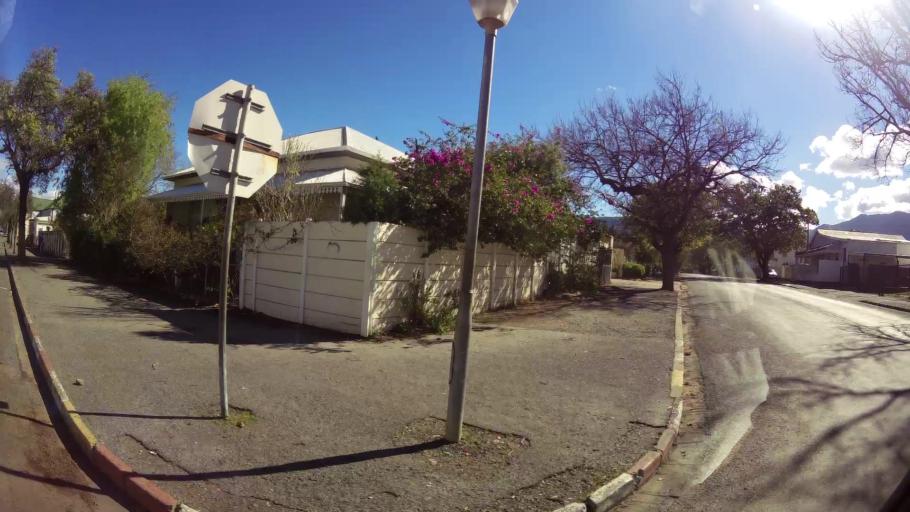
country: ZA
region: Western Cape
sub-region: Cape Winelands District Municipality
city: Ashton
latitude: -33.8007
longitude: 19.8817
